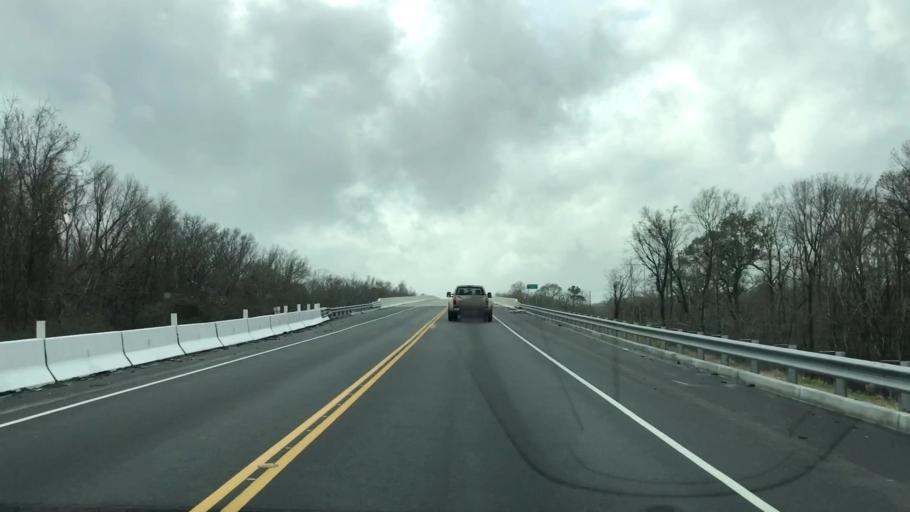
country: US
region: South Carolina
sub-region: Horry County
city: Socastee
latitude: 33.6629
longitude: -79.1512
